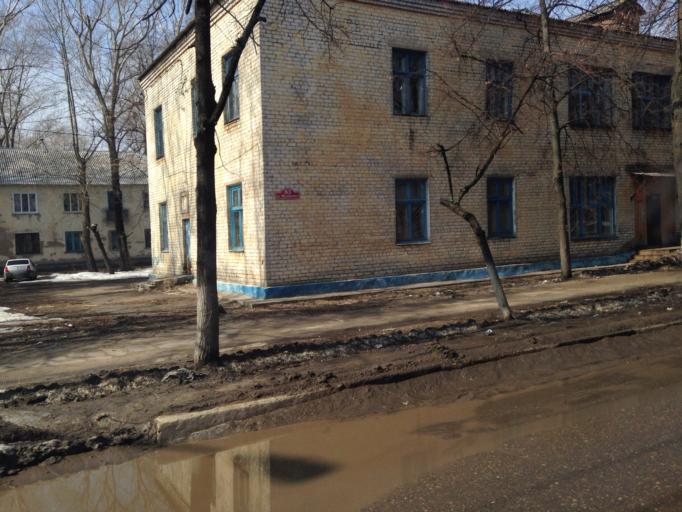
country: RU
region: Ulyanovsk
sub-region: Ulyanovskiy Rayon
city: Ulyanovsk
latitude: 54.3491
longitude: 48.5481
